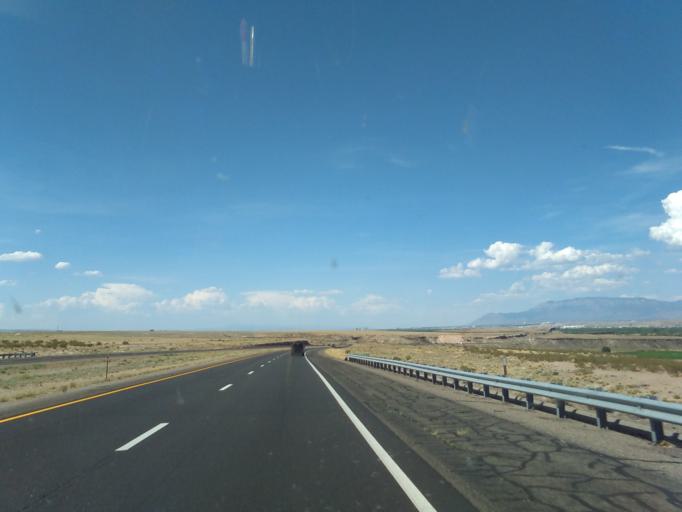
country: US
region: New Mexico
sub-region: Valencia County
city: Bosque Farms
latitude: 34.9270
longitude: -106.7177
